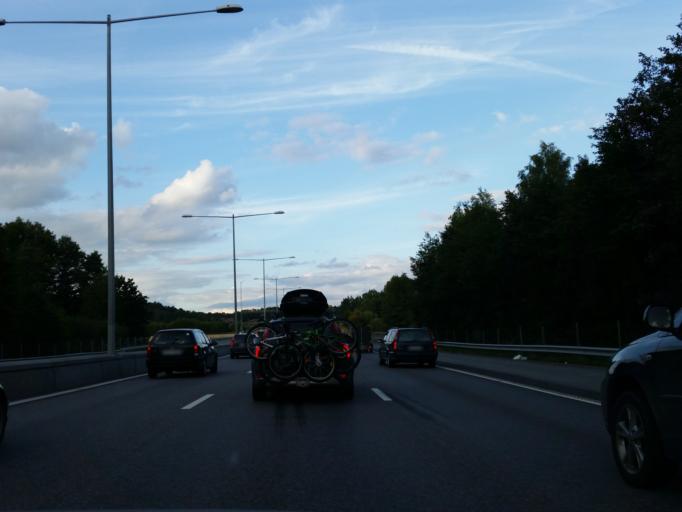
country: SE
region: Stockholm
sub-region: Botkyrka Kommun
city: Eriksberg
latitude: 59.2335
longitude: 17.8078
